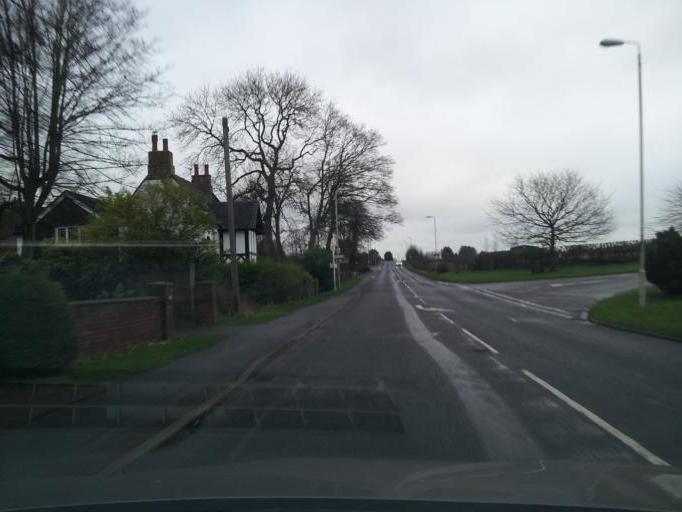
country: GB
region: England
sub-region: Leicestershire
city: Donisthorpe
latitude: 52.7431
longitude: -1.5198
